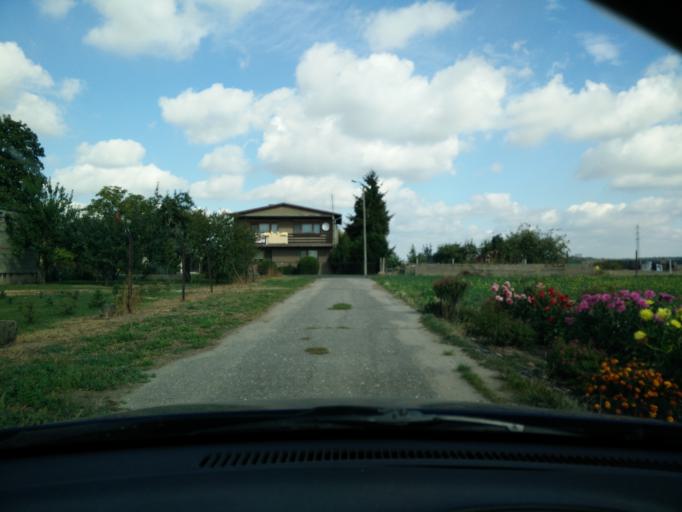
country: PL
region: Greater Poland Voivodeship
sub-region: Powiat sredzki
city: Dominowo
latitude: 52.2884
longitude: 17.3877
